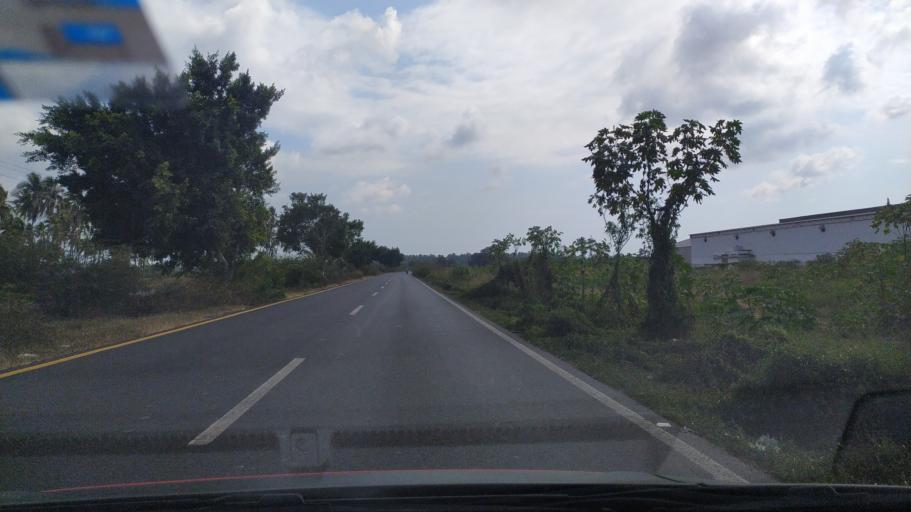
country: MX
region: Colima
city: Tecoman
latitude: 18.9170
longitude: -103.8542
